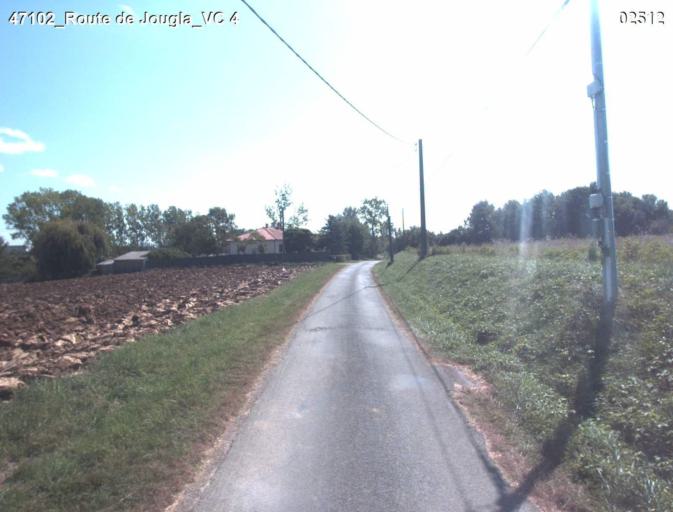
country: FR
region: Aquitaine
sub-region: Departement du Lot-et-Garonne
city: Nerac
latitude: 44.0612
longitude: 0.4272
